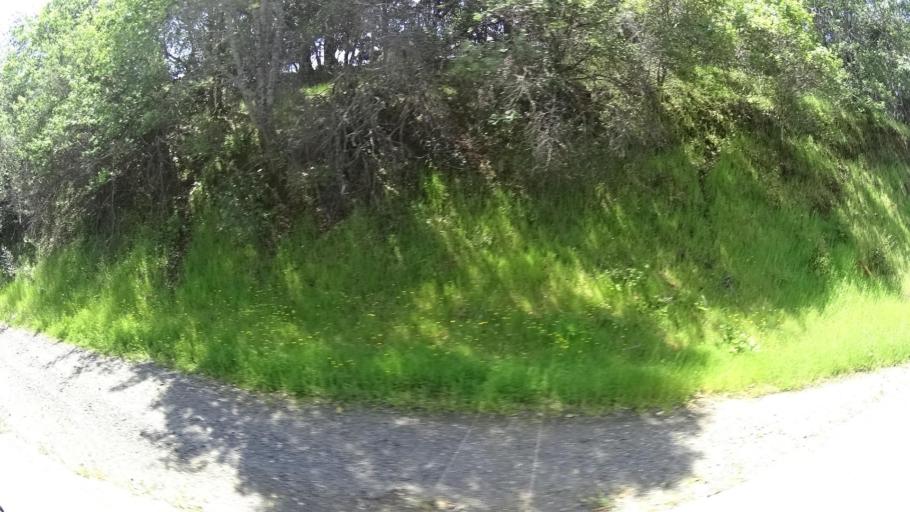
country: US
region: California
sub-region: Humboldt County
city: Redway
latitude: 40.1752
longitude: -123.6015
